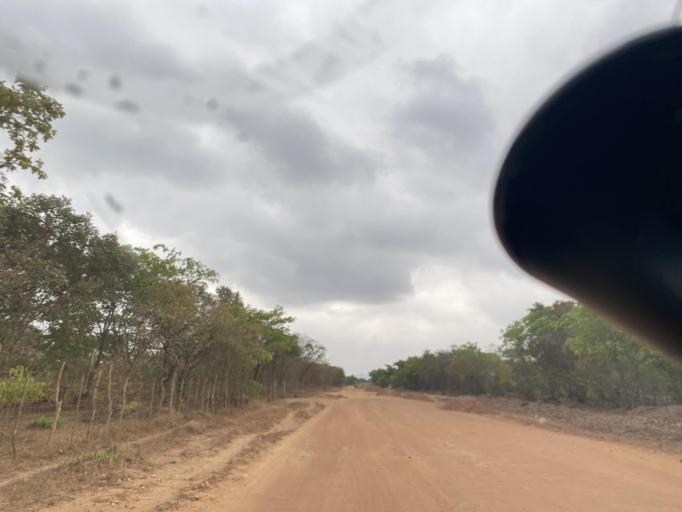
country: ZM
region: Lusaka
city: Chongwe
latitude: -15.2660
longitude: 28.7319
